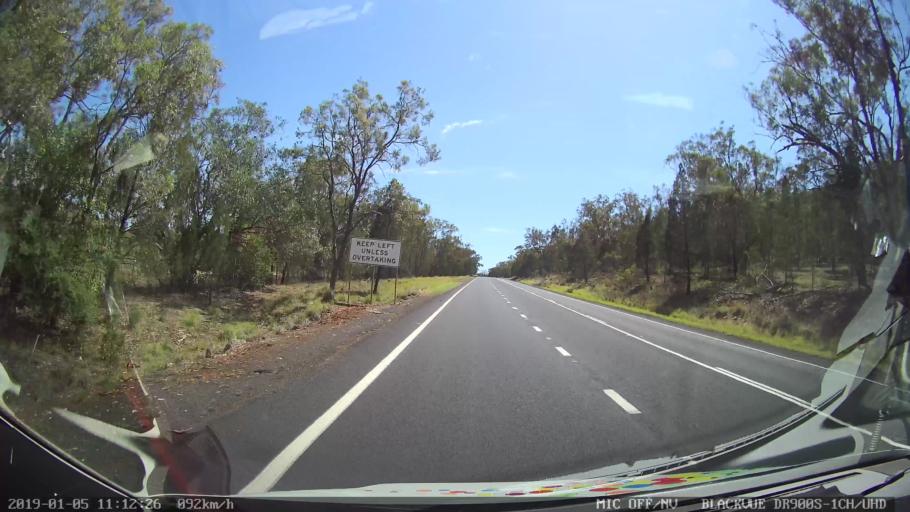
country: AU
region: New South Wales
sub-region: Warrumbungle Shire
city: Coonabarabran
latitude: -31.3820
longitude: 149.2608
